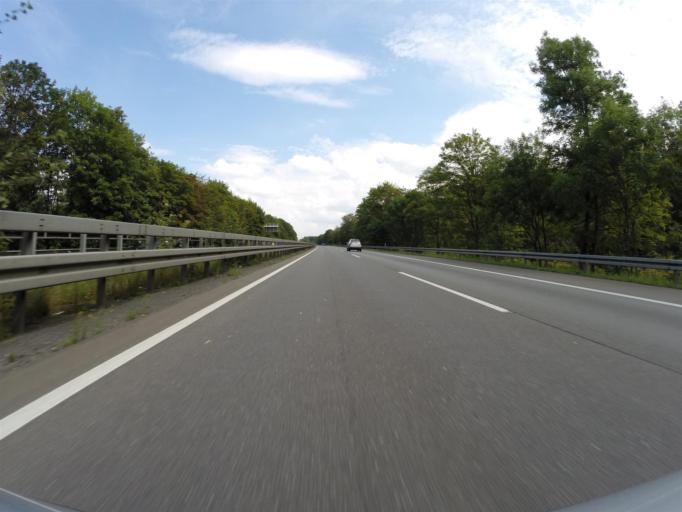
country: DE
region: North Rhine-Westphalia
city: Marsberg
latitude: 51.5364
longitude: 8.8826
